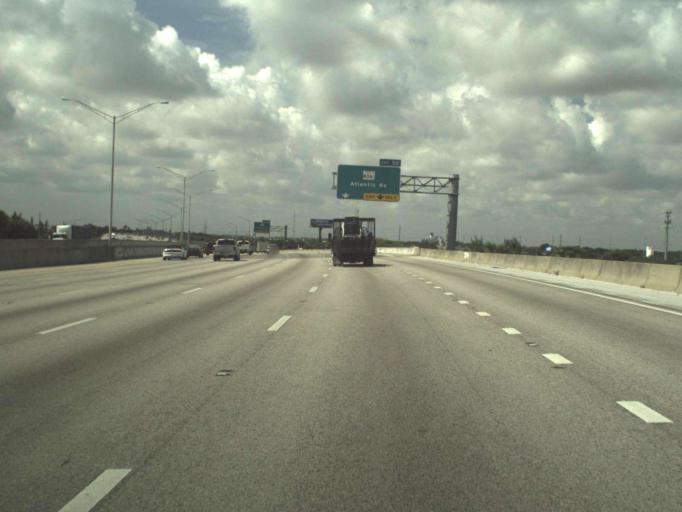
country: US
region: Florida
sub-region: Palm Beach County
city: Delray Beach
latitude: 26.4704
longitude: -80.0895
